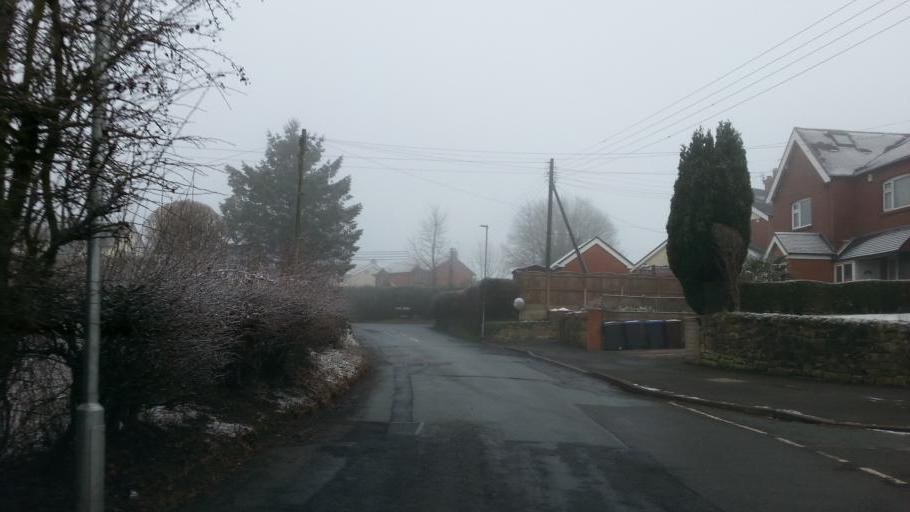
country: GB
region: England
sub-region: Staffordshire
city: Biddulph
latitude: 53.1247
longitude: -2.1802
